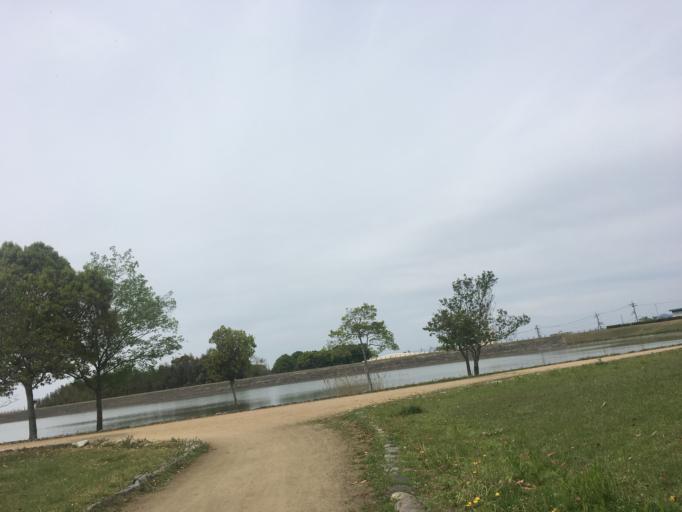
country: JP
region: Hyogo
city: Miki
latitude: 34.7667
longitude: 134.9230
